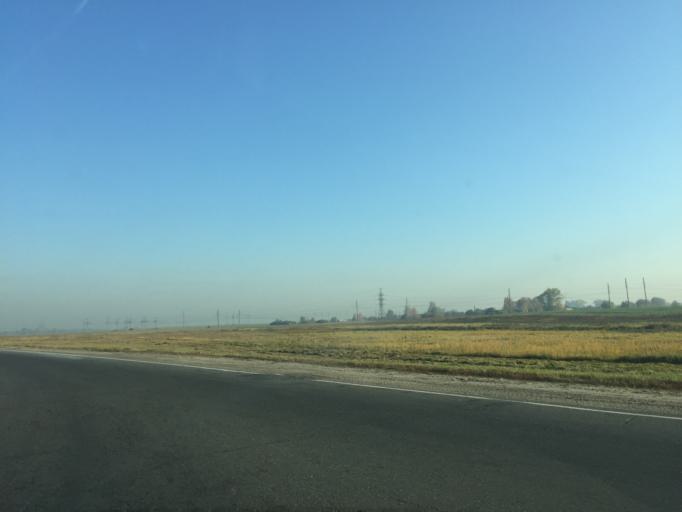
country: BY
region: Gomel
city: Kastsyukowka
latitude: 52.4524
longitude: 30.8253
